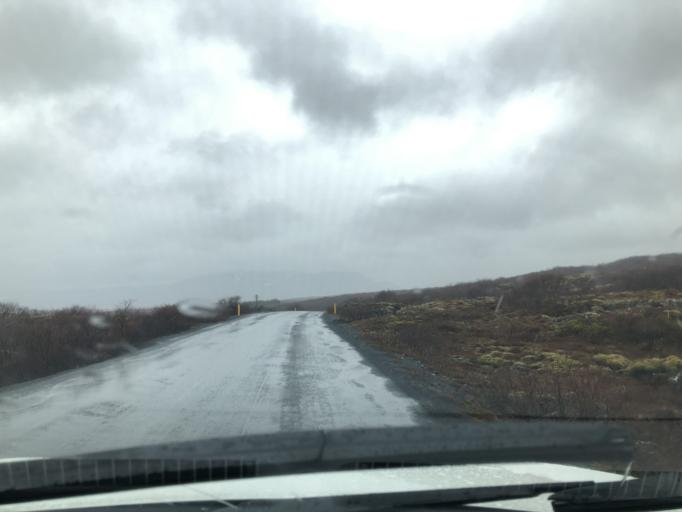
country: IS
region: South
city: Hveragerdi
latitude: 64.2374
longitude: -21.0289
